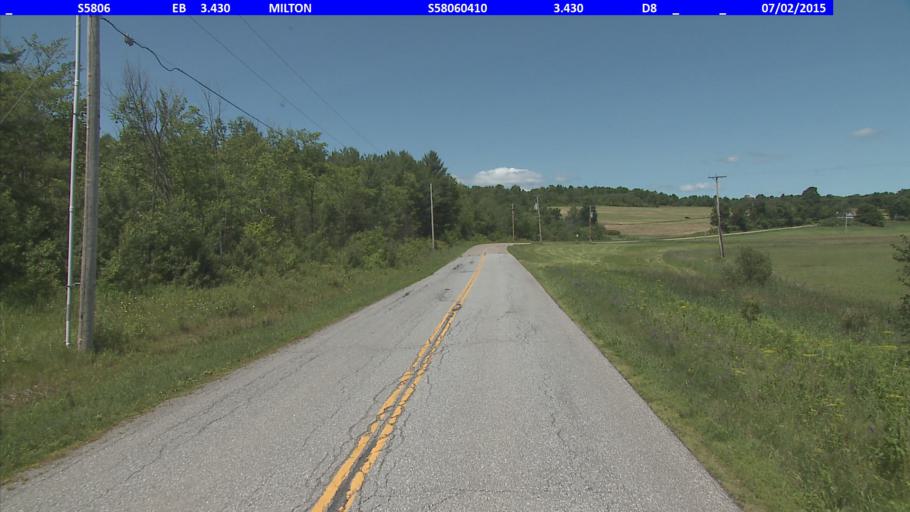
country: US
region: Vermont
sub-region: Chittenden County
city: Milton
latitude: 44.6716
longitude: -73.1741
